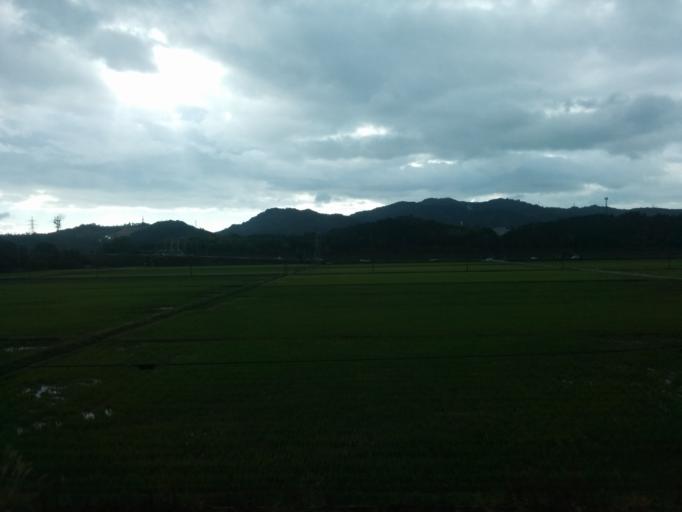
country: JP
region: Shiga Prefecture
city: Omihachiman
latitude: 35.0946
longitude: 136.0635
